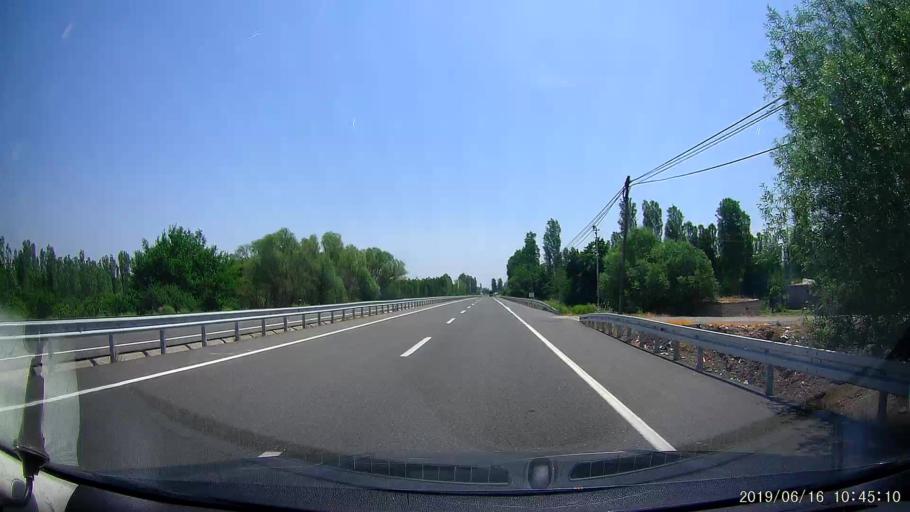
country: AM
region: Armavir
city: Shenavan
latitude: 40.0281
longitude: 43.8657
